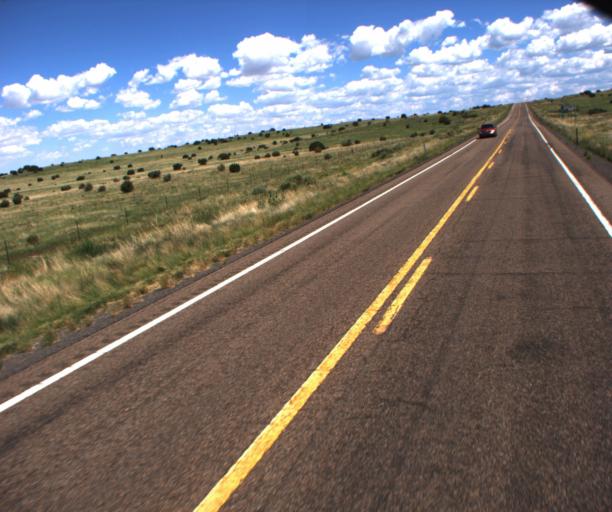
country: US
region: Arizona
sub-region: Apache County
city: Springerville
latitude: 34.2477
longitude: -109.5314
